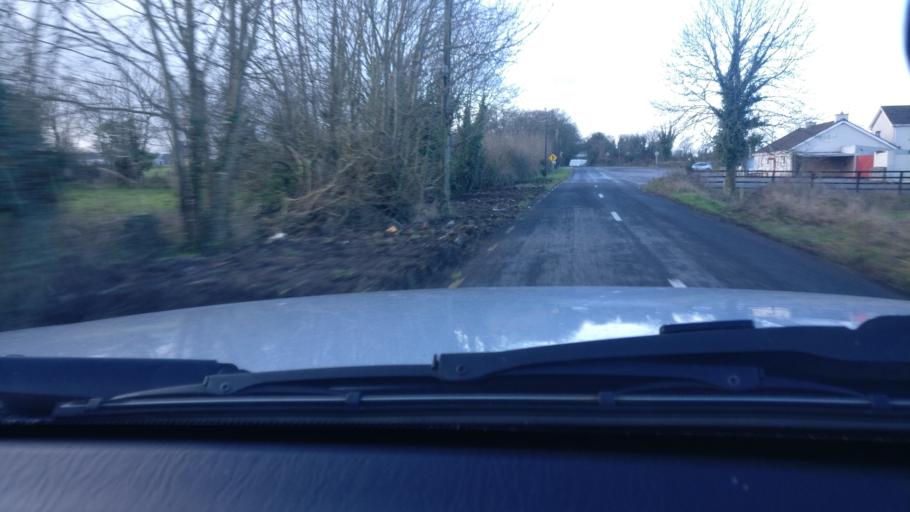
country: IE
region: Connaught
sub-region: County Galway
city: Ballinasloe
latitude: 53.2288
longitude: -8.3464
